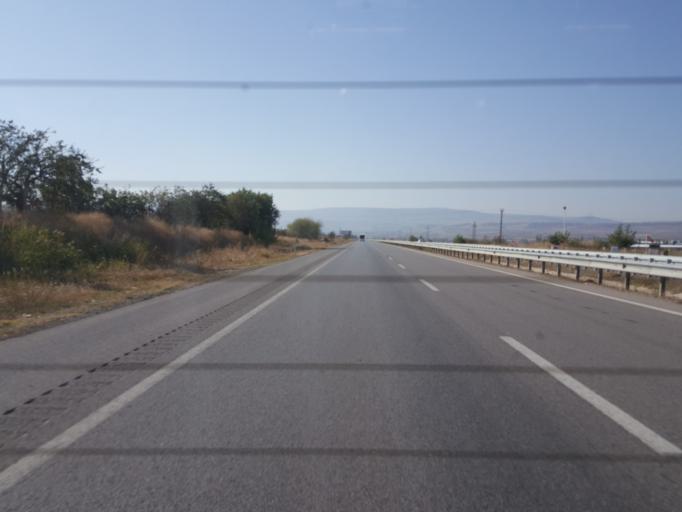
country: TR
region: Amasya
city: Merzifon
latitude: 40.8202
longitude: 35.4583
